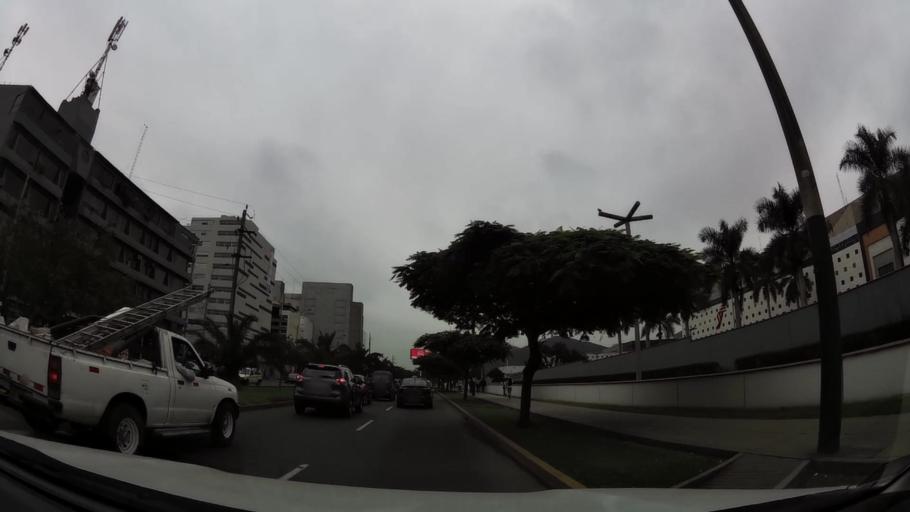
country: PE
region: Lima
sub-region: Lima
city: La Molina
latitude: -12.1013
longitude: -76.9700
